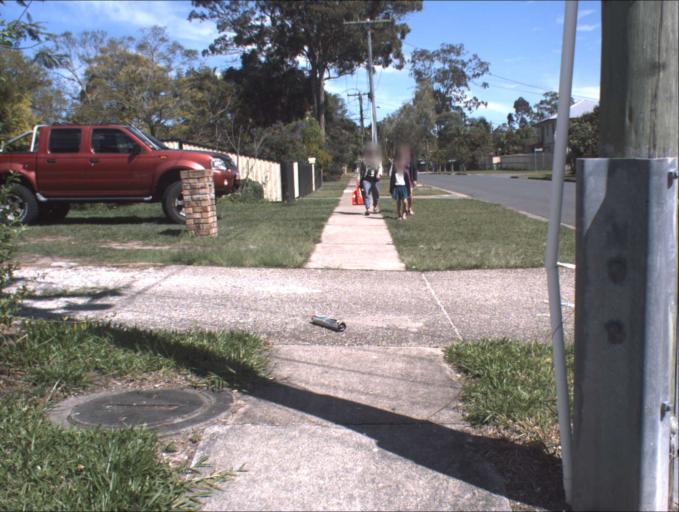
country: AU
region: Queensland
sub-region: Logan
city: Waterford West
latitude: -27.6808
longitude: 153.1099
